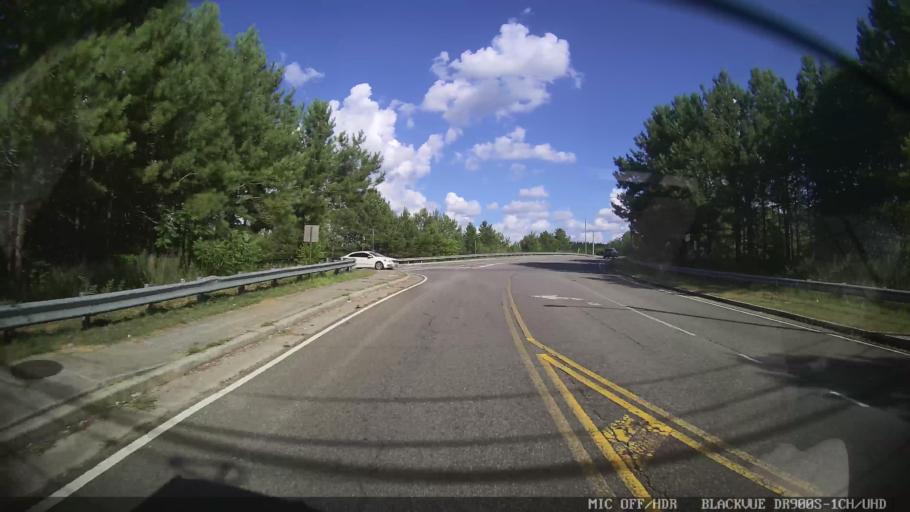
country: US
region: Georgia
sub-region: Floyd County
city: Rome
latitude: 34.2208
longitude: -85.1334
